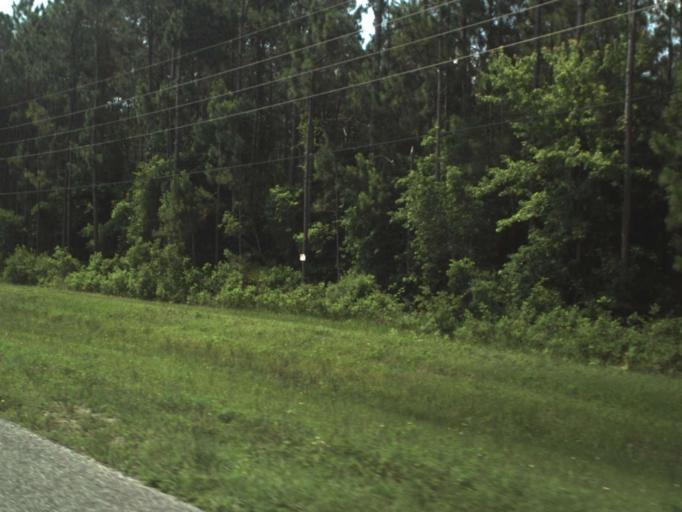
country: US
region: Florida
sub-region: Volusia County
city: Samsula-Spruce Creek
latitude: 29.0224
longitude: -81.1152
